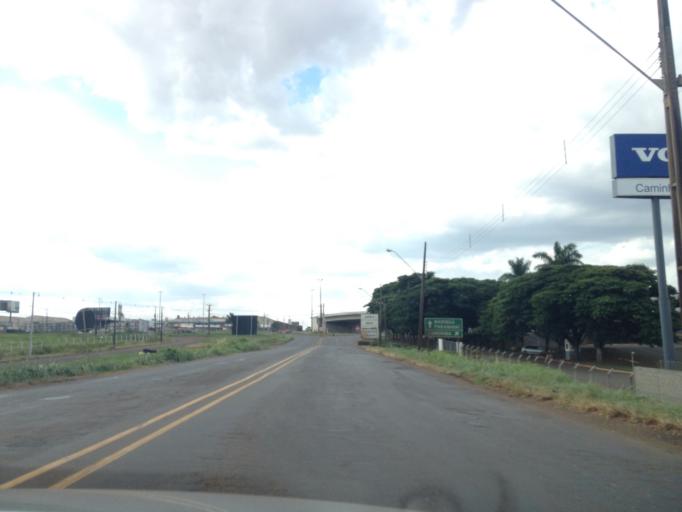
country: BR
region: Parana
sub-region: Sarandi
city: Sarandi
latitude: -23.4341
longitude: -51.8885
